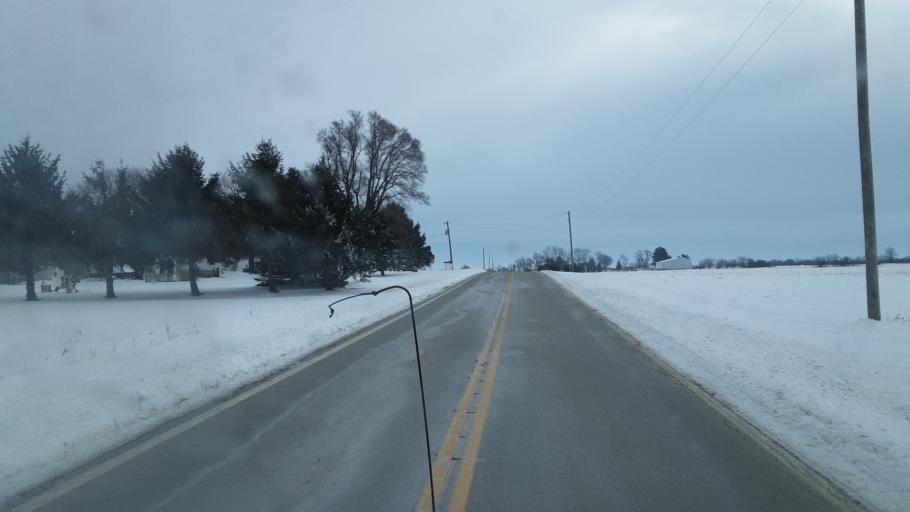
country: US
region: Ohio
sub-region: Madison County
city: Choctaw Lake
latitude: 40.0162
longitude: -83.5122
